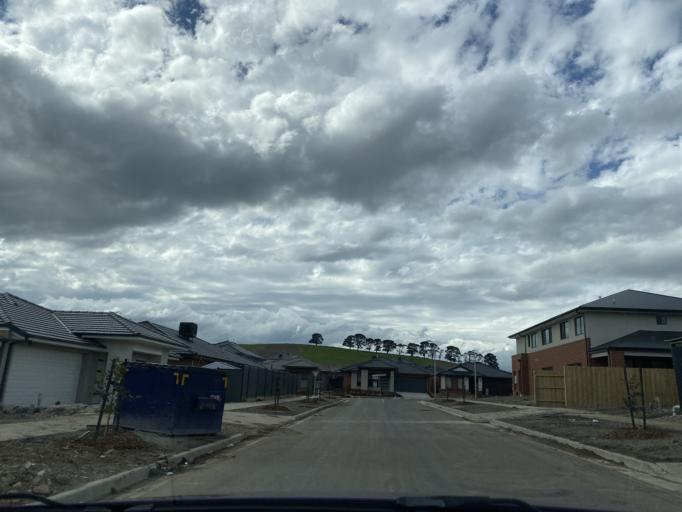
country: AU
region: Victoria
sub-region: Whittlesea
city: Mernda
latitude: -37.5973
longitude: 145.0757
